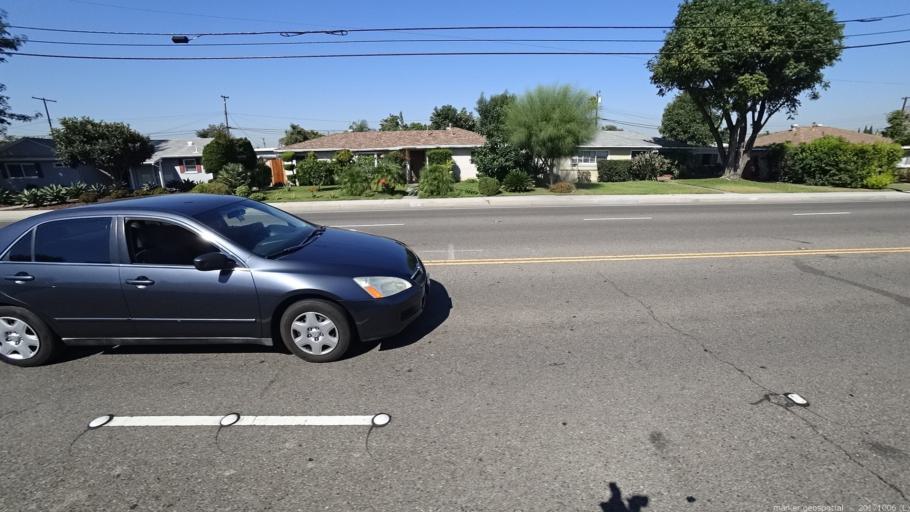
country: US
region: California
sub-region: Orange County
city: Stanton
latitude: 33.7884
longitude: -117.9820
